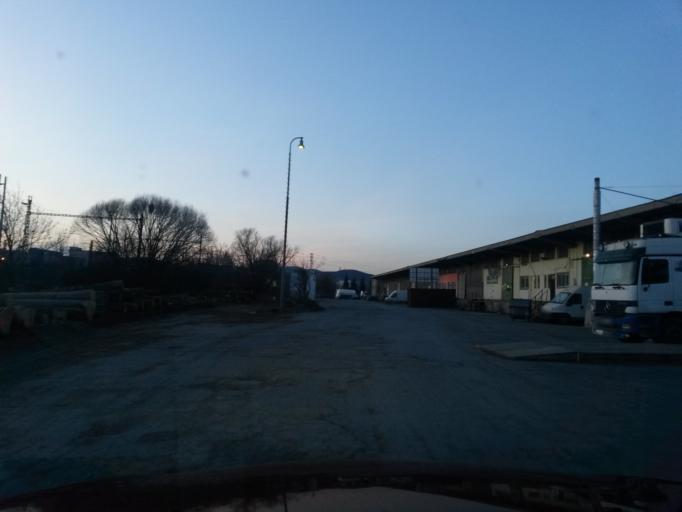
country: SK
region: Kosicky
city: Kosice
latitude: 48.7179
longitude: 21.2737
